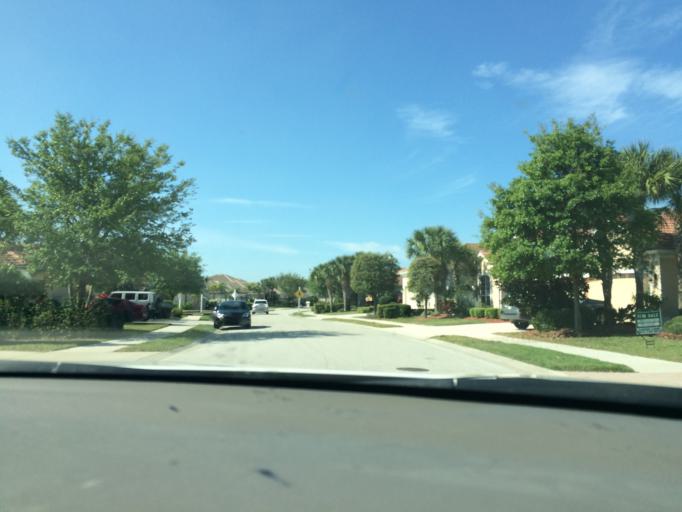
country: US
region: Florida
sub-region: Sarasota County
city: The Meadows
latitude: 27.4246
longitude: -82.3896
